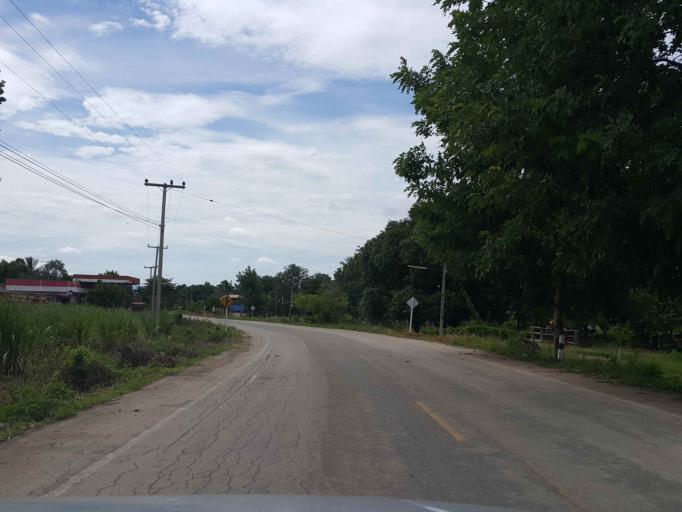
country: TH
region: Sukhothai
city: Ban Dan Lan Hoi
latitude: 17.0772
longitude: 99.4796
